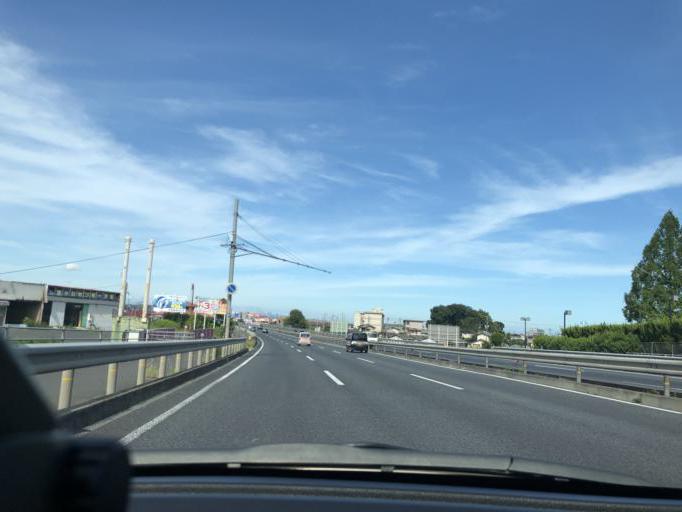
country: JP
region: Okayama
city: Kurashiki
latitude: 34.5864
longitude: 133.7900
